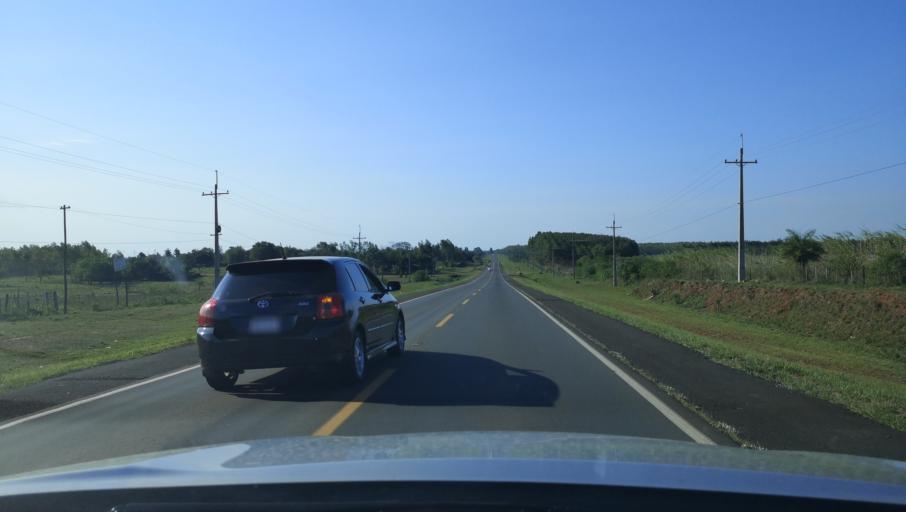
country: PY
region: Misiones
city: Santa Maria
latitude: -26.7771
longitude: -57.0288
